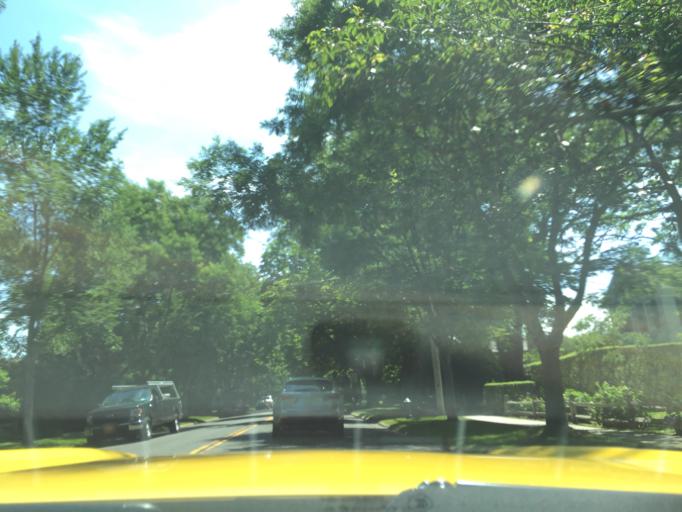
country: US
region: New York
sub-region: Suffolk County
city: East Hampton
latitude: 40.9594
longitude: -72.1997
